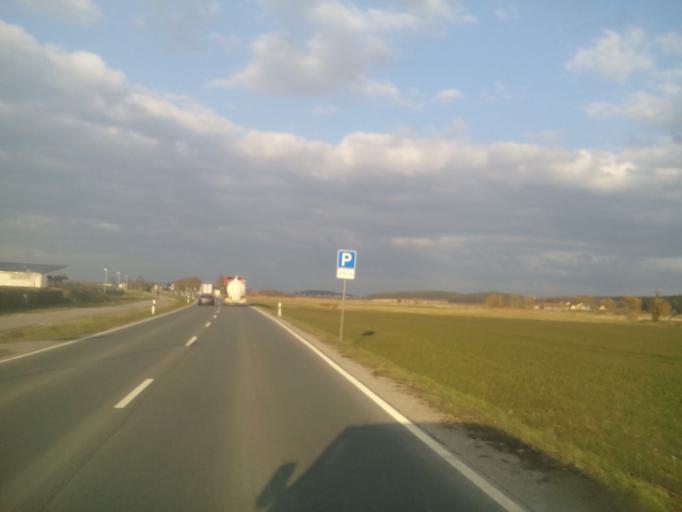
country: DE
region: Bavaria
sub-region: Regierungsbezirk Mittelfranken
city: Uehlfeld
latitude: 49.6735
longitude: 10.7288
